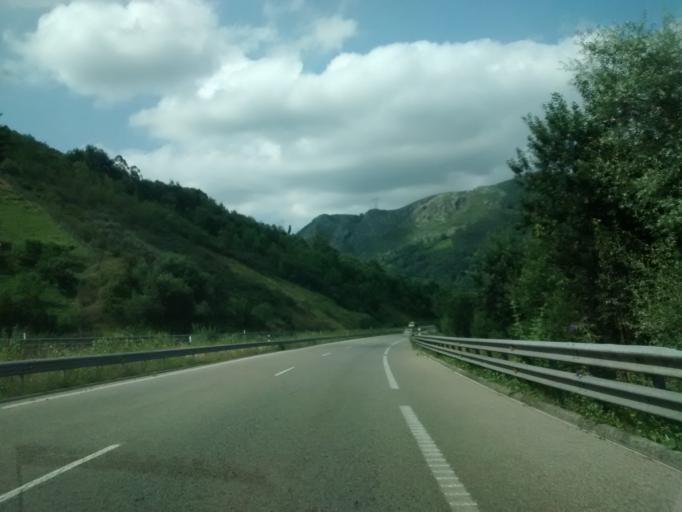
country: ES
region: Asturias
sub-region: Province of Asturias
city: Sama
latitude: 43.3165
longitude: -5.7452
